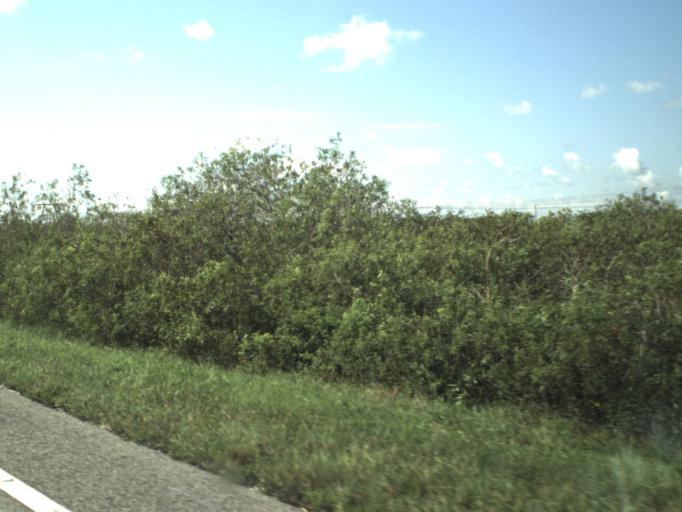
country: US
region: Florida
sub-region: Broward County
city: Weston
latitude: 26.3032
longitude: -80.5136
